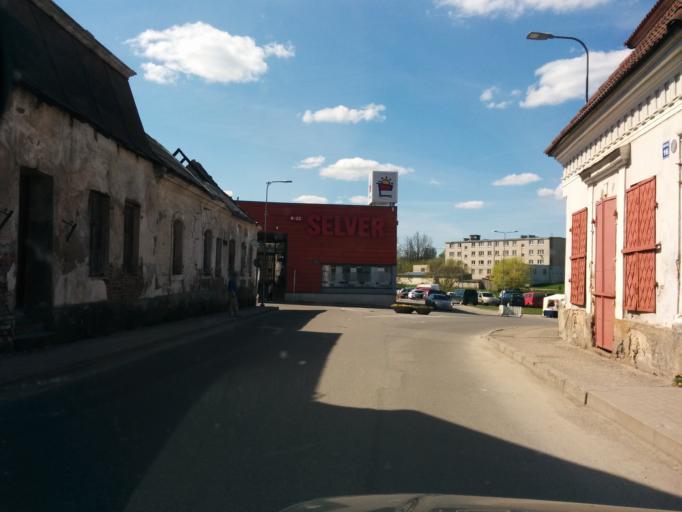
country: LV
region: Valkas Rajons
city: Valka
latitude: 57.7773
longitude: 26.0284
